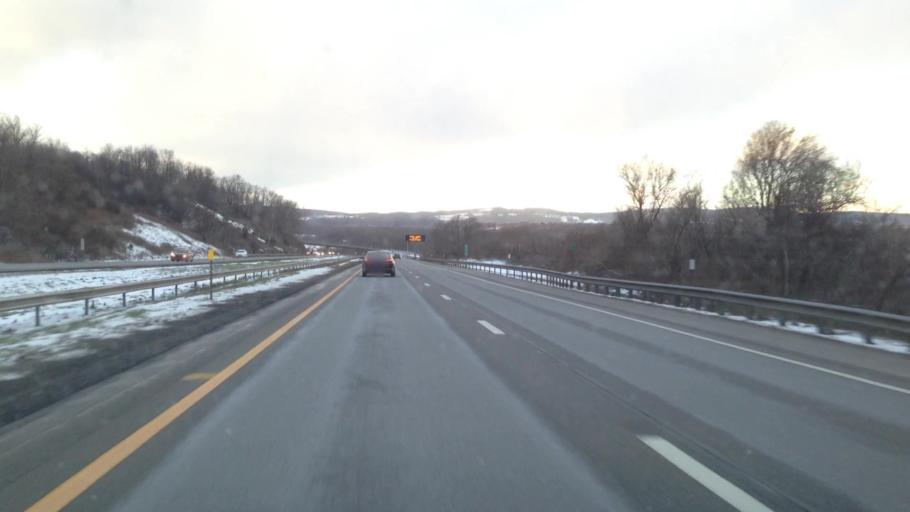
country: US
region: New York
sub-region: Herkimer County
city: Little Falls
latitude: 43.0115
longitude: -74.9172
